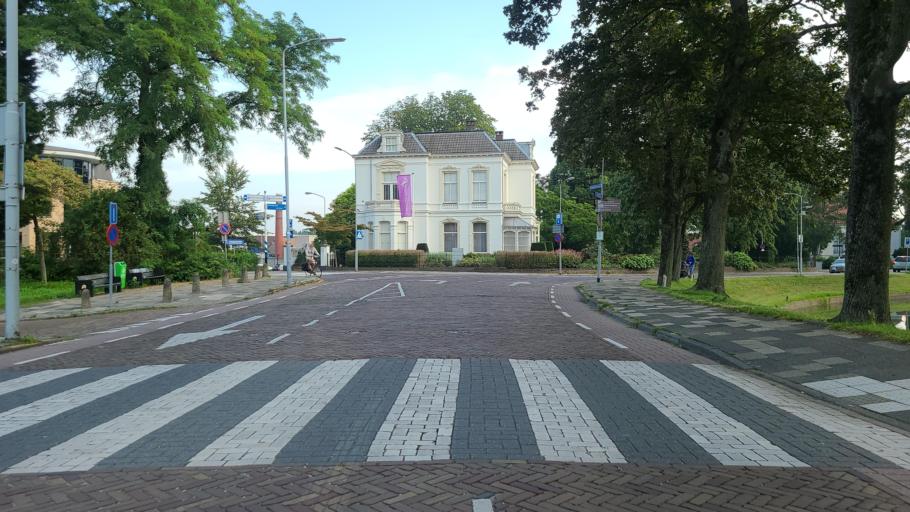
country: NL
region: Gelderland
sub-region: Gemeente Tiel
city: Tiel
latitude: 51.8886
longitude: 5.4312
